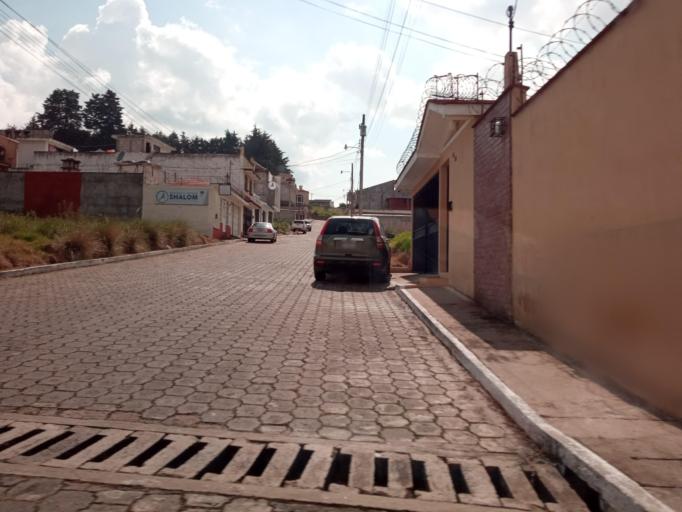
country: GT
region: Quetzaltenango
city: Quetzaltenango
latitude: 14.8491
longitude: -91.5423
